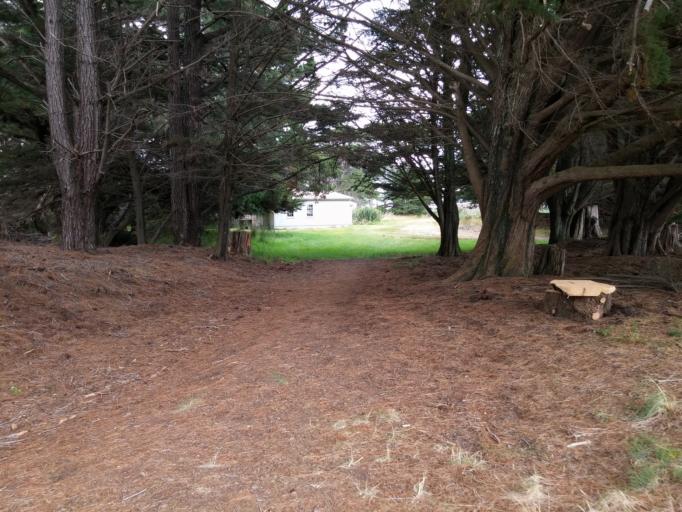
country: NZ
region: Tasman
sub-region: Tasman District
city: Takaka
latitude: -40.5465
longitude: 173.0085
